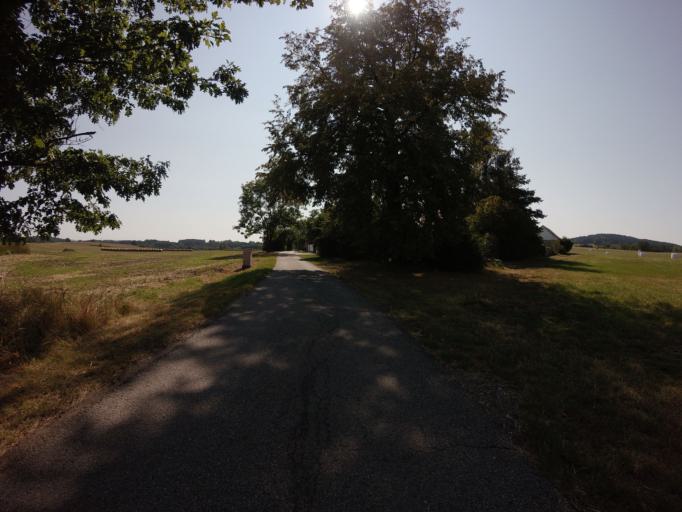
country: CZ
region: Jihocesky
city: Kamenny Ujezd
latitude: 48.8806
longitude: 14.3899
